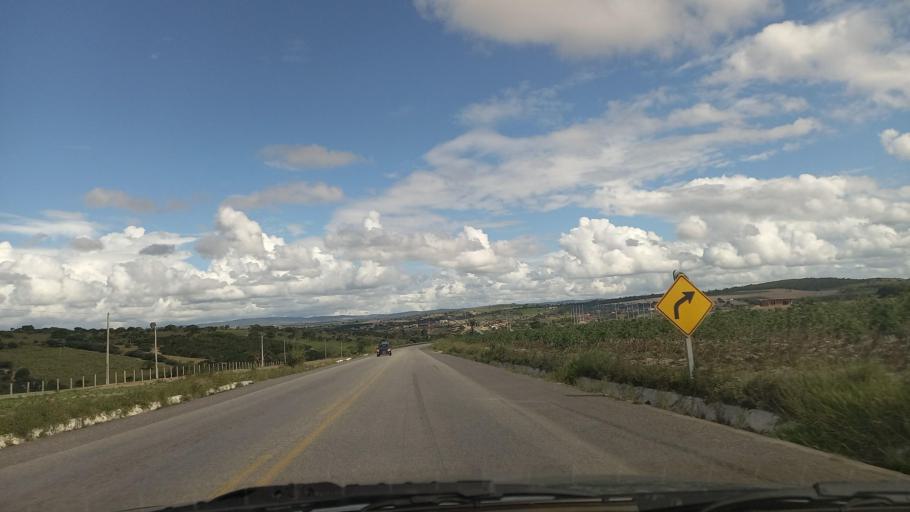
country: BR
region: Pernambuco
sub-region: Lajedo
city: Lajedo
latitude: -8.7378
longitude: -36.4309
